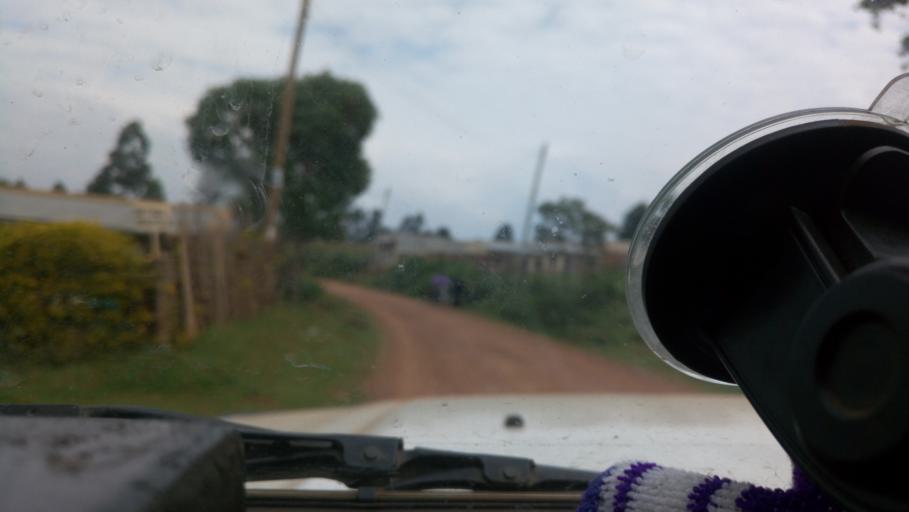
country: KE
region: Kericho
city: Litein
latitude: -0.6210
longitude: 35.1927
